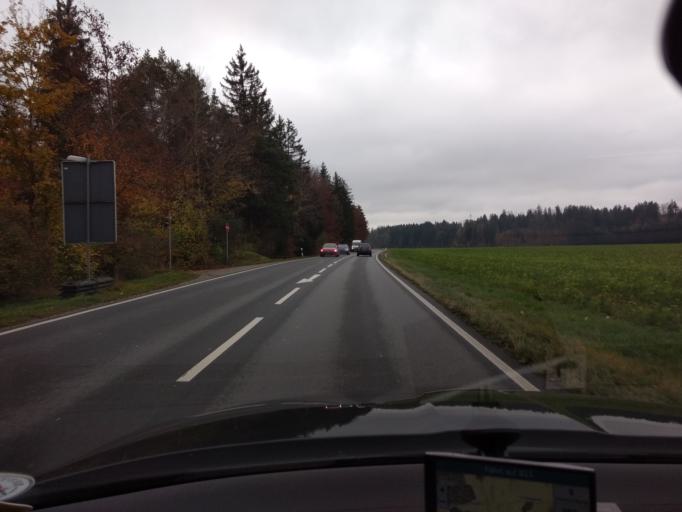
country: DE
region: Bavaria
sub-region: Upper Bavaria
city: Geretsried
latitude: 47.8695
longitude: 11.4701
